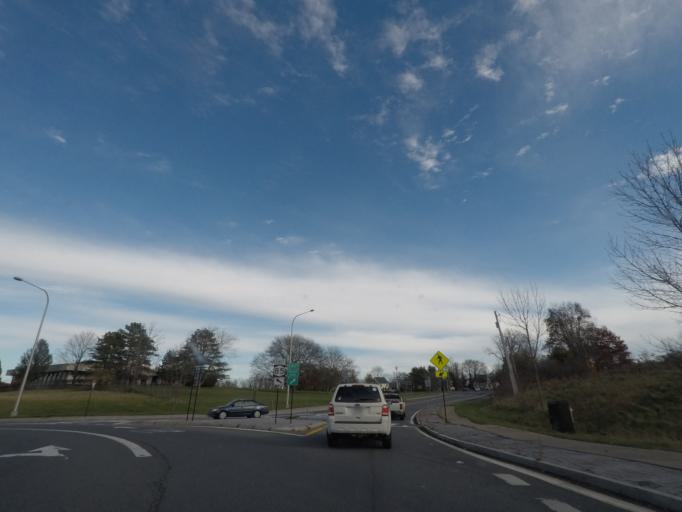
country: US
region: New York
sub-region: Albany County
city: Delmar
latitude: 42.6447
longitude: -73.8527
